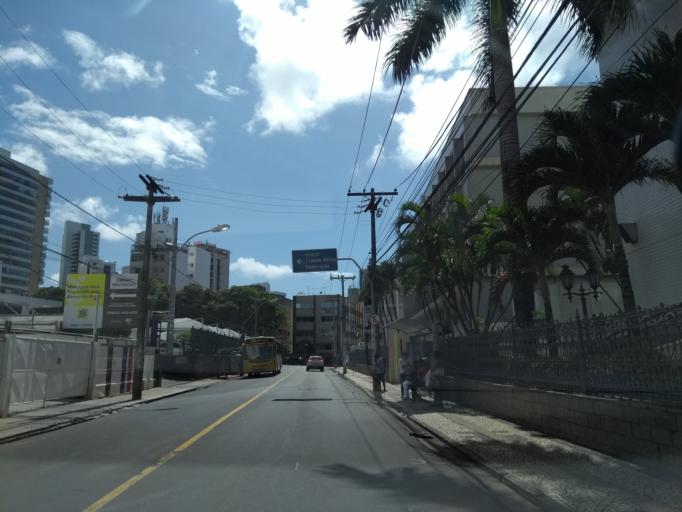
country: BR
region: Bahia
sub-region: Salvador
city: Salvador
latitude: -13.0025
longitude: -38.5250
